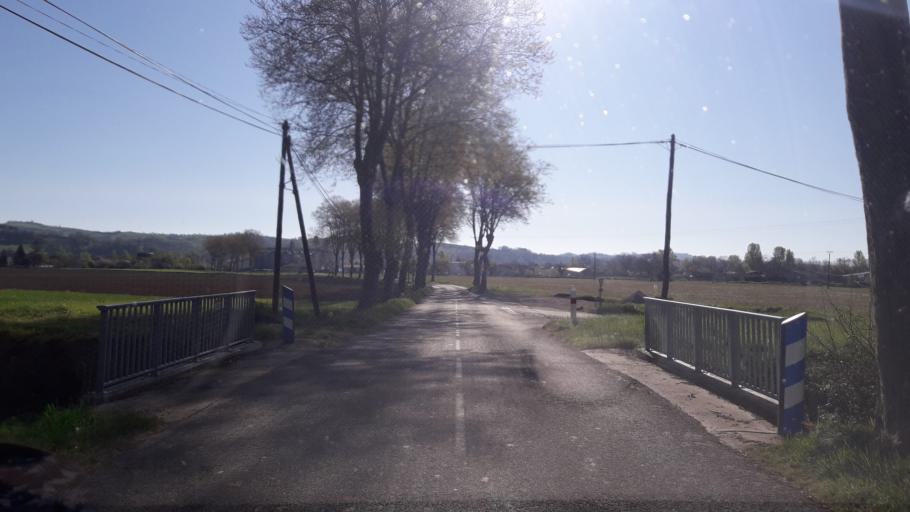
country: FR
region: Midi-Pyrenees
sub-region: Departement de la Haute-Garonne
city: Montesquieu-Volvestre
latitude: 43.2043
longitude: 1.2171
